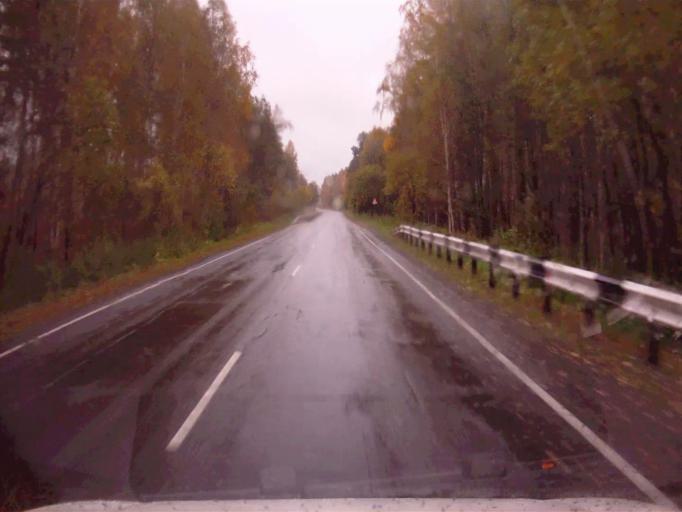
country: RU
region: Chelyabinsk
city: Verkhniy Ufaley
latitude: 55.9412
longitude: 60.4098
